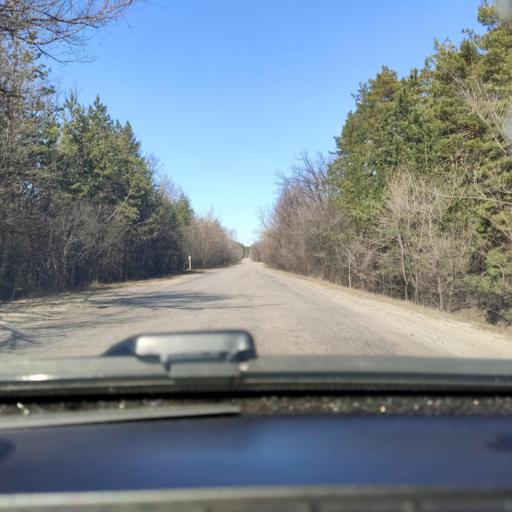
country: RU
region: Voronezj
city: Somovo
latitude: 51.7171
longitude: 39.3668
